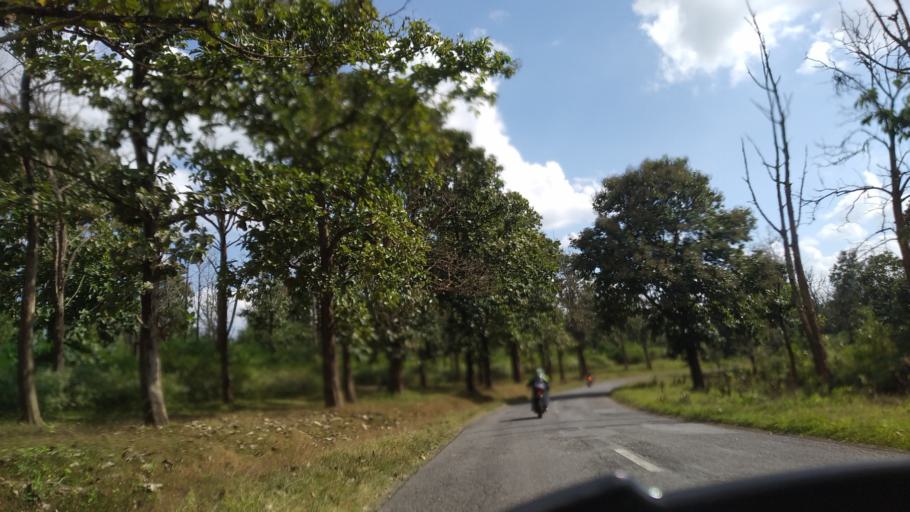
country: IN
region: Kerala
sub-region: Wayanad
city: Panamaram
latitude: 11.9226
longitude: 76.0659
